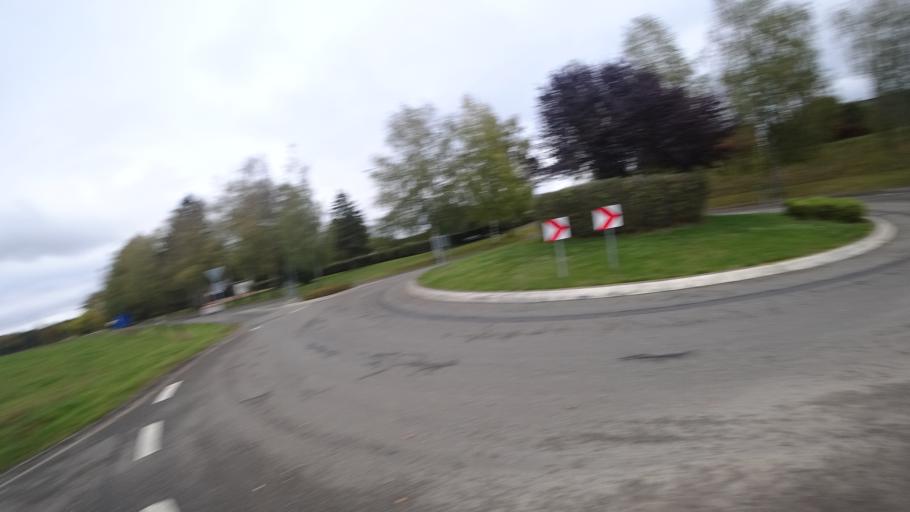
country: DE
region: Rheinland-Pfalz
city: Sessenhausen
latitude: 50.5318
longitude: 7.7131
